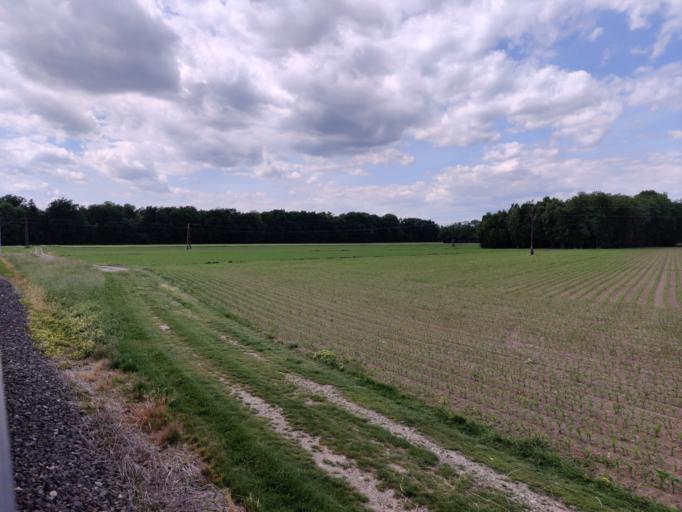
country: AT
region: Styria
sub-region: Politischer Bezirk Suedoststeiermark
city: Eichfeld
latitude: 46.7130
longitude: 15.7462
